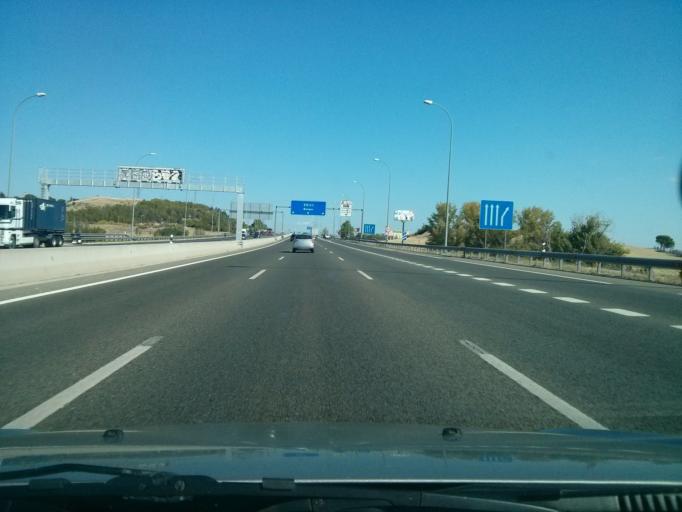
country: ES
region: Madrid
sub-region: Provincia de Madrid
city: San Sebastian de los Reyes
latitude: 40.5748
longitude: -3.5861
